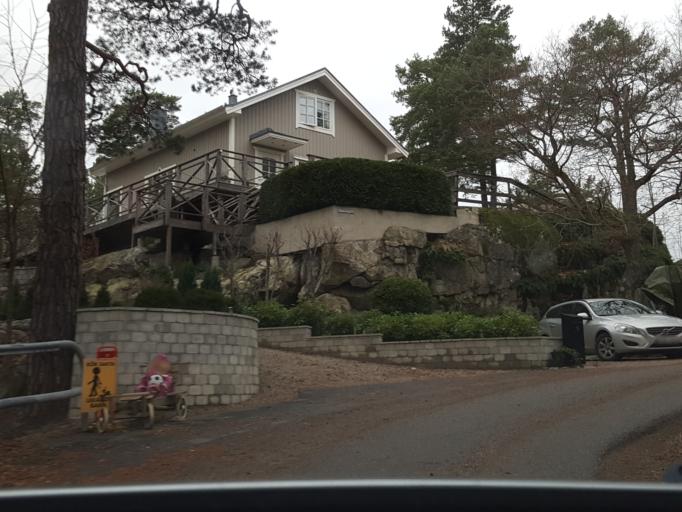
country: SE
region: Stockholm
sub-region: Nacka Kommun
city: Boo
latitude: 59.3233
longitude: 18.2872
